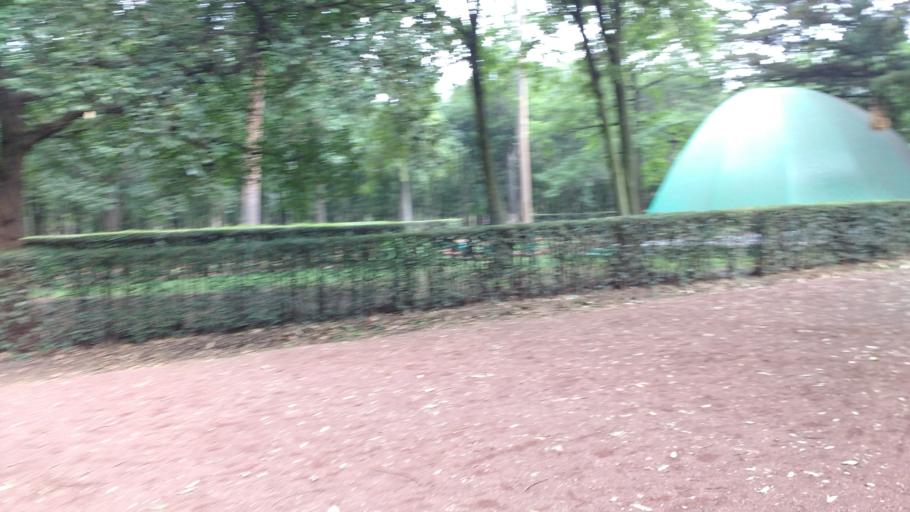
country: MX
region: Mexico City
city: Coyoacan
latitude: 19.3554
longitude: -99.1710
